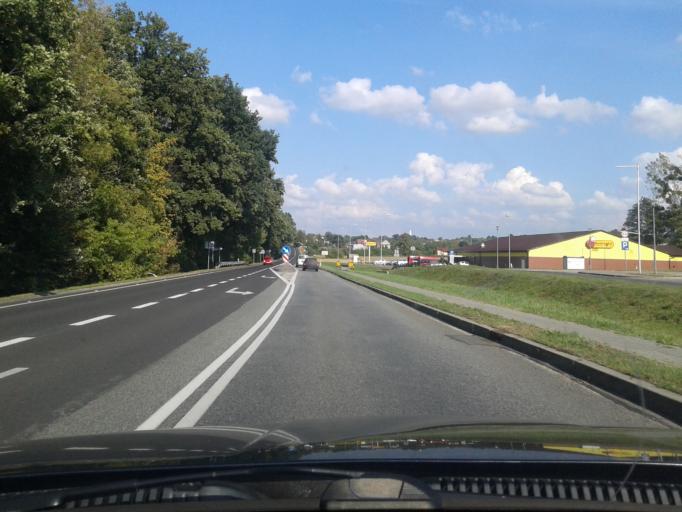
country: PL
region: Silesian Voivodeship
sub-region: Powiat wodzislawski
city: Gorzyce
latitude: 49.9557
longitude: 18.3743
